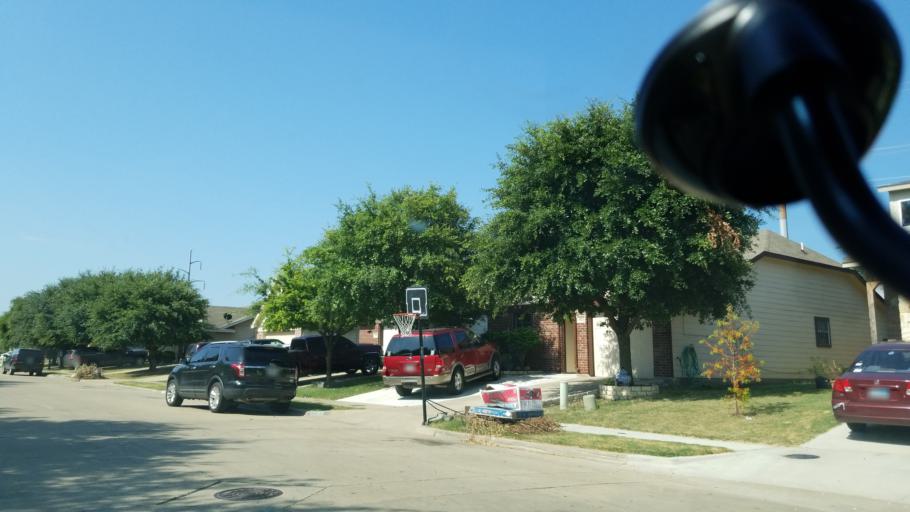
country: US
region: Texas
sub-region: Dallas County
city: Cockrell Hill
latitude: 32.7102
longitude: -96.8736
